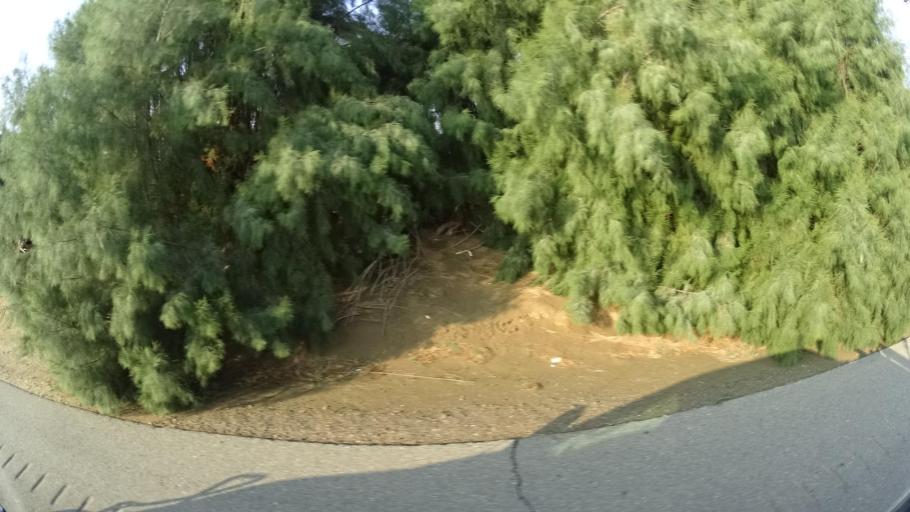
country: US
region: California
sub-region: Kern County
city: Weedpatch
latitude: 35.1330
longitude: -118.9147
